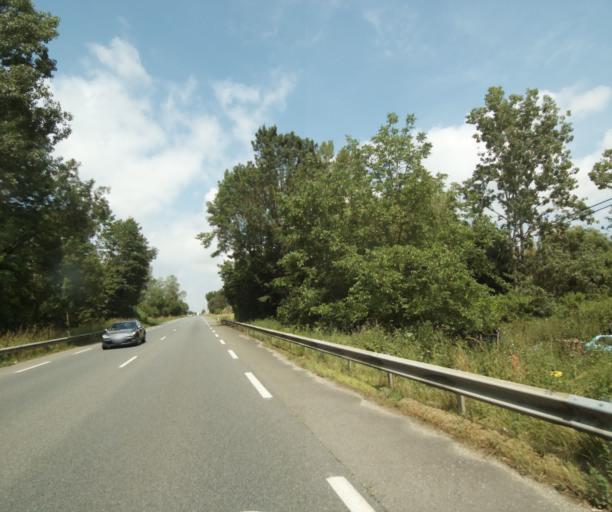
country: FR
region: Midi-Pyrenees
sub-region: Departement du Tarn-et-Garonne
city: Albias
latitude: 44.0723
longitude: 1.4244
